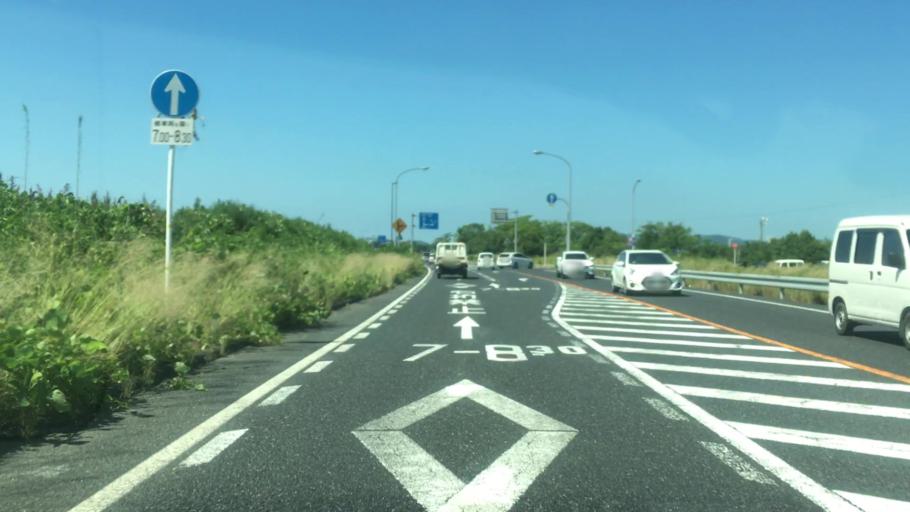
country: JP
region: Tottori
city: Tottori
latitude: 35.4499
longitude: 134.2141
